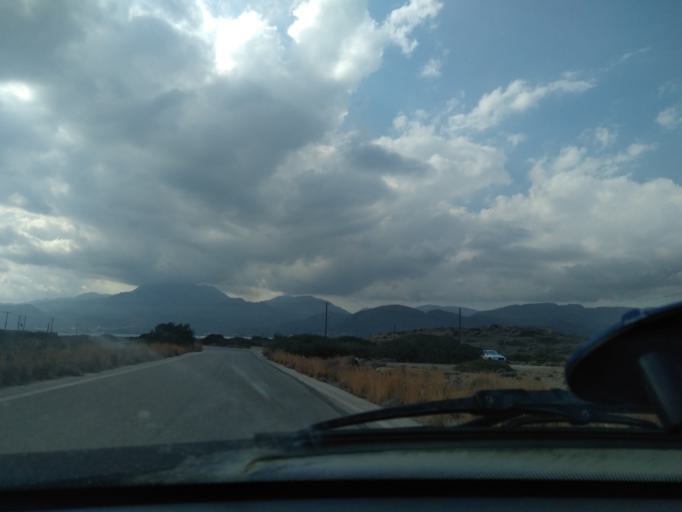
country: GR
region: Crete
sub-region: Nomos Lasithiou
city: Makry-Gialos
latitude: 35.0249
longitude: 26.0122
